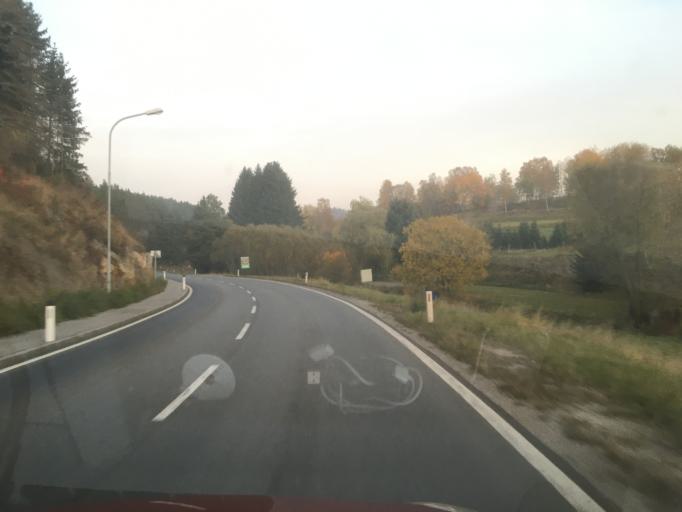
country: AT
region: Lower Austria
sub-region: Politischer Bezirk Zwettl
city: Gross-Gerungs
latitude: 48.5723
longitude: 14.9655
